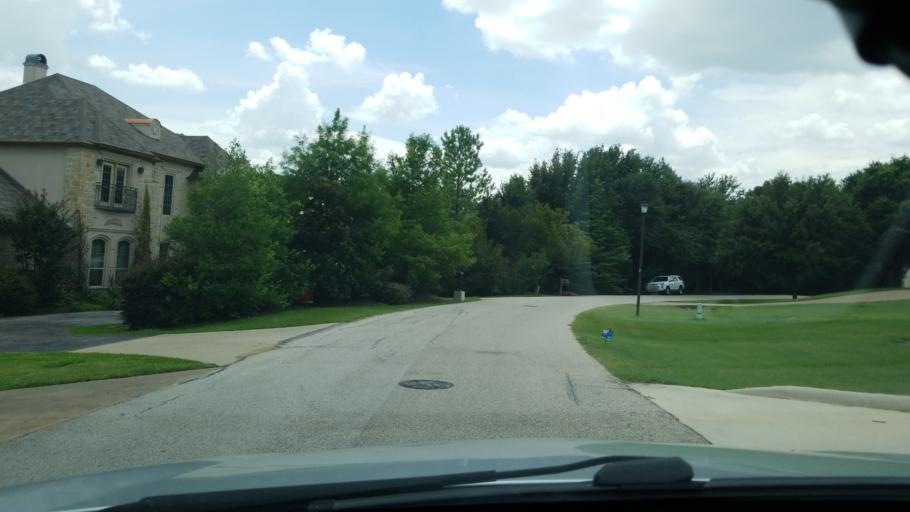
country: US
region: Texas
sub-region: Dallas County
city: Coppell
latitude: 32.9567
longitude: -96.9784
